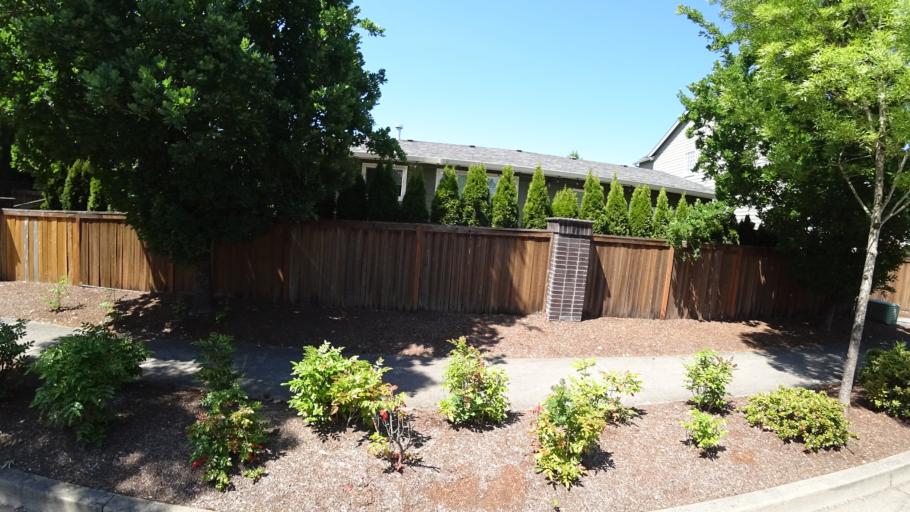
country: US
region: Oregon
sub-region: Washington County
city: Rockcreek
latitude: 45.5202
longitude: -122.9260
